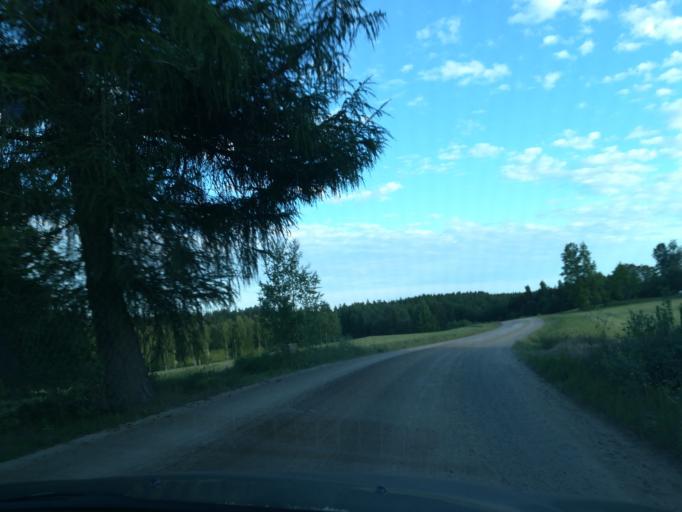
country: FI
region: Southern Savonia
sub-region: Mikkeli
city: Puumala
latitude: 61.5900
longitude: 28.1166
